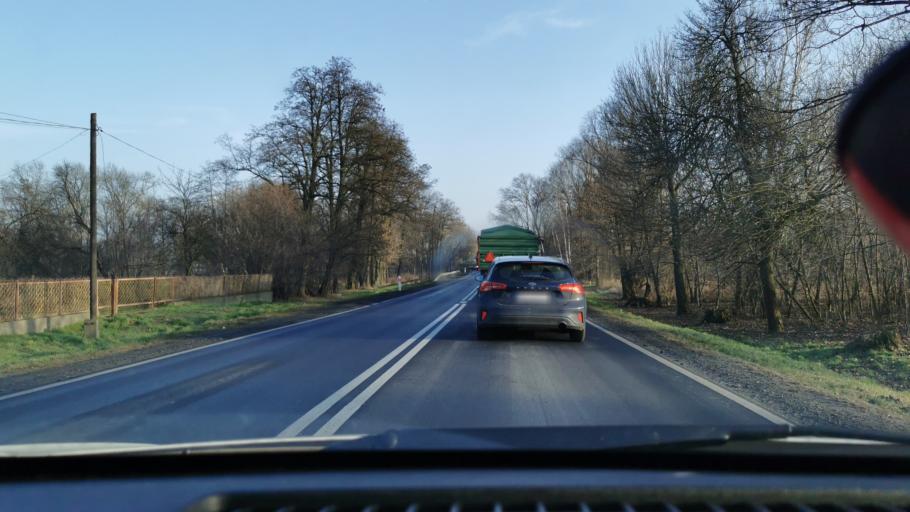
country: PL
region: Lodz Voivodeship
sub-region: Powiat sieradzki
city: Wroblew
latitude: 51.6129
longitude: 18.6119
